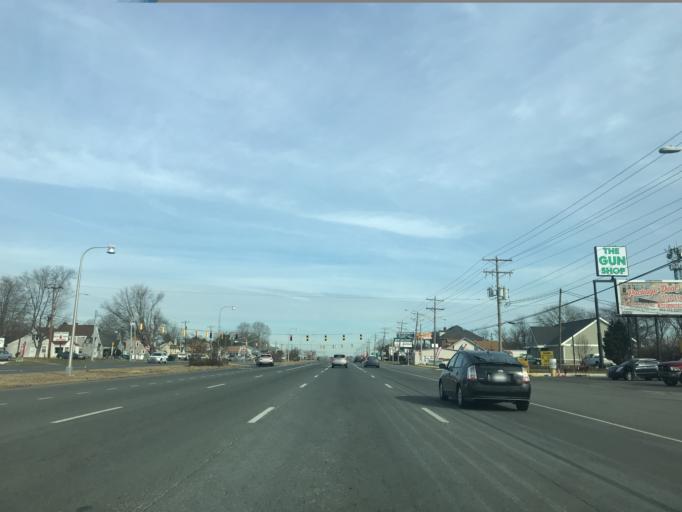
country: US
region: Delaware
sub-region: New Castle County
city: Wilmington Manor
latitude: 39.6568
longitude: -75.6137
